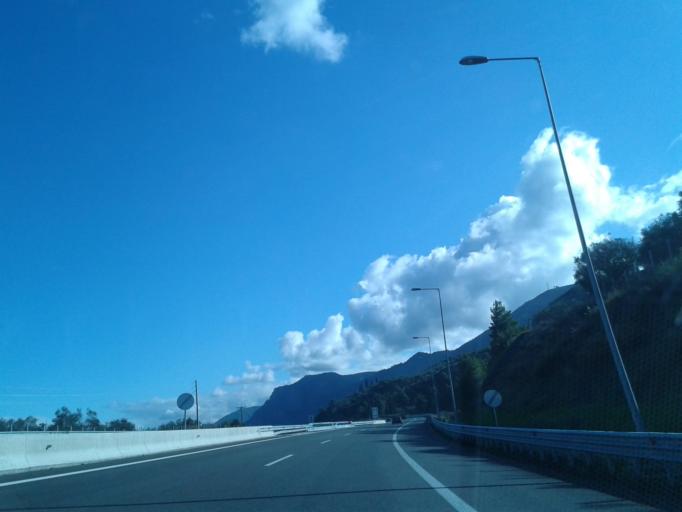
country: GR
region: West Greece
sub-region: Nomos Achaias
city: Temeni
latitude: 38.2076
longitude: 22.1365
